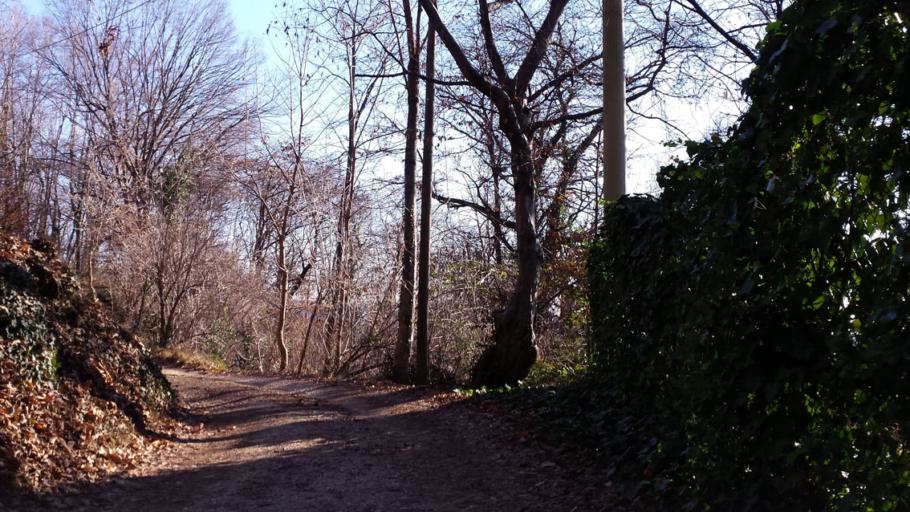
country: IT
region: Veneto
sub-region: Provincia di Treviso
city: Paderno del Grappa
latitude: 45.8361
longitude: 11.8646
